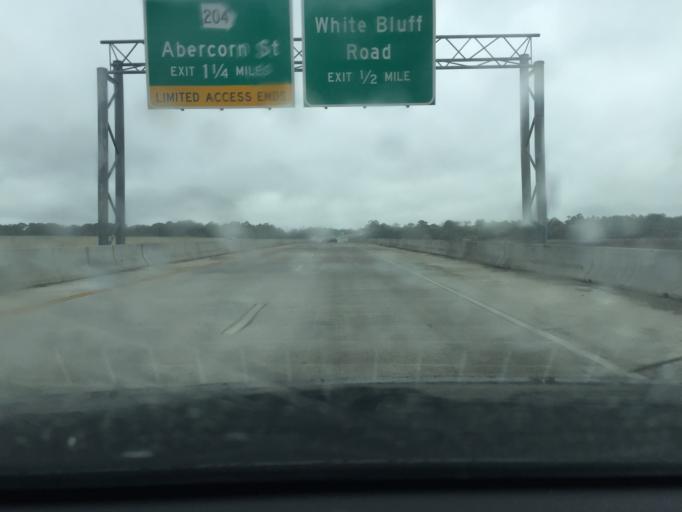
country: US
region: Georgia
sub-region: Chatham County
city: Montgomery
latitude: 31.9752
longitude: -81.1188
